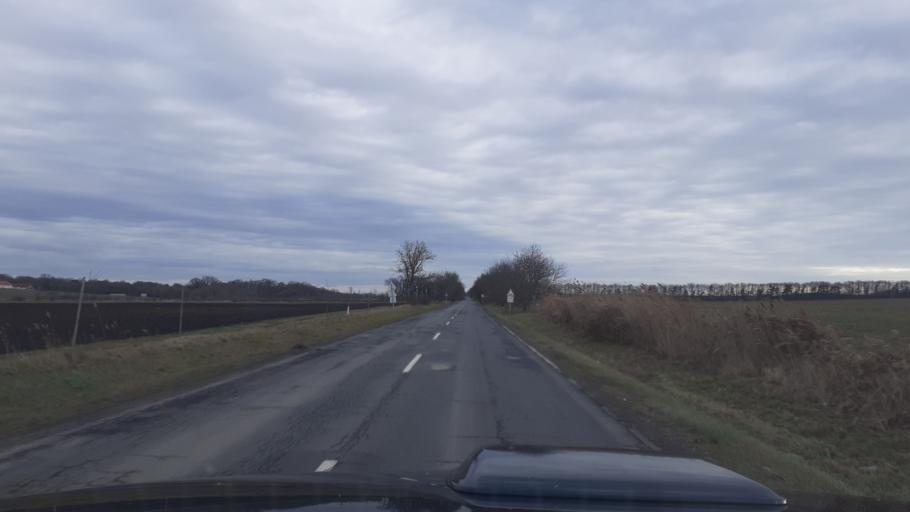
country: HU
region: Fejer
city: Mezofalva
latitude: 46.9796
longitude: 18.7165
